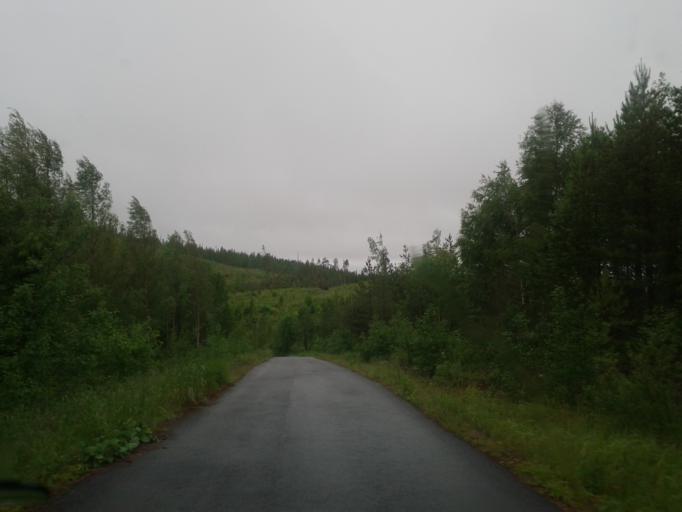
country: SE
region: Vaesternorrland
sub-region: Ange Kommun
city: Fransta
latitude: 62.3845
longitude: 16.3180
